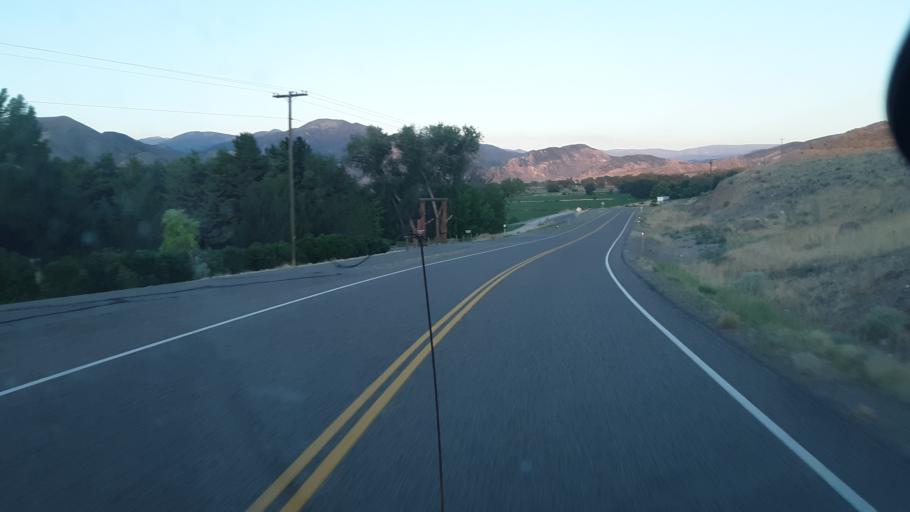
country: US
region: Utah
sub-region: Sevier County
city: Monroe
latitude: 38.6055
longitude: -112.2284
